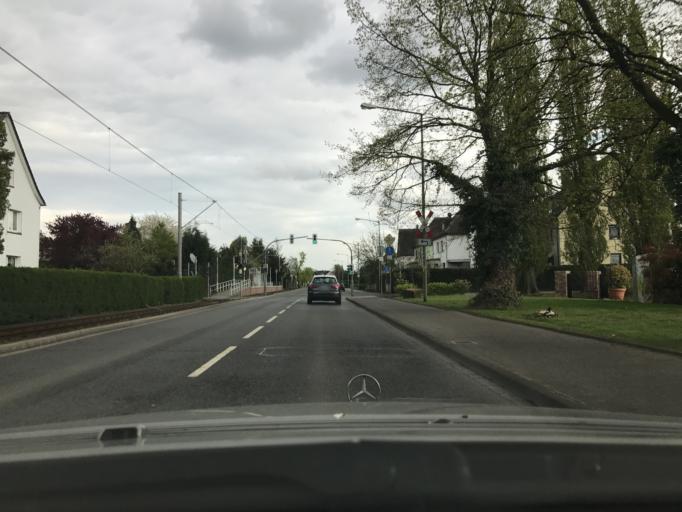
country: DE
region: North Rhine-Westphalia
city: Waltrop
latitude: 51.5858
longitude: 7.4459
